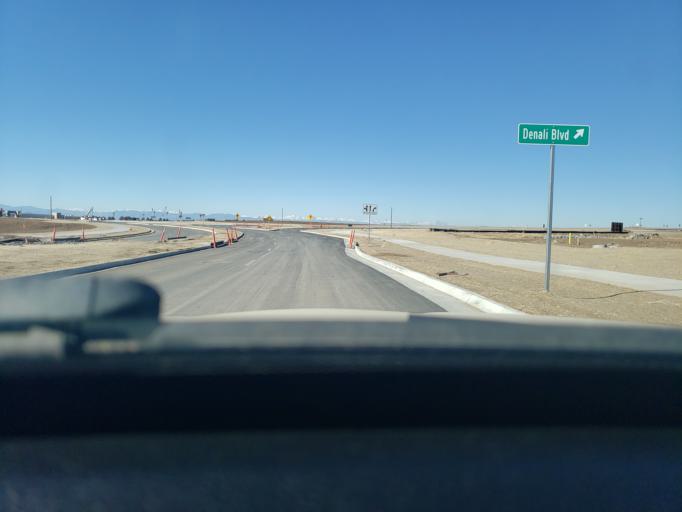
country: US
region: Colorado
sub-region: Adams County
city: Aurora
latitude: 39.7703
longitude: -104.7046
